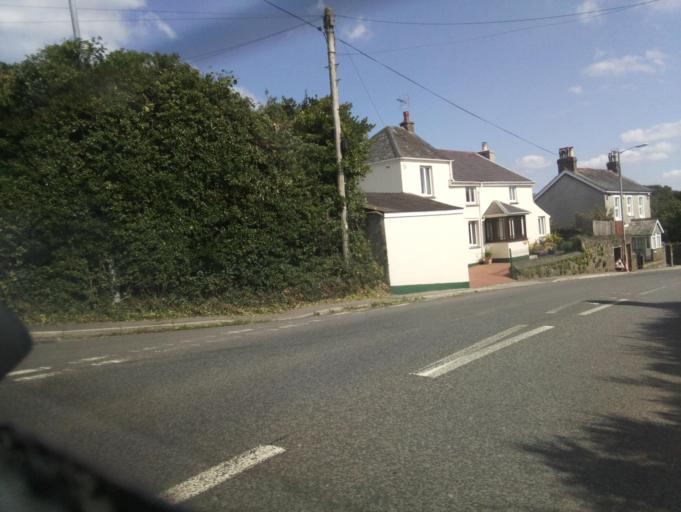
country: GB
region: England
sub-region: Cornwall
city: Saltash
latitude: 50.4226
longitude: -4.2380
